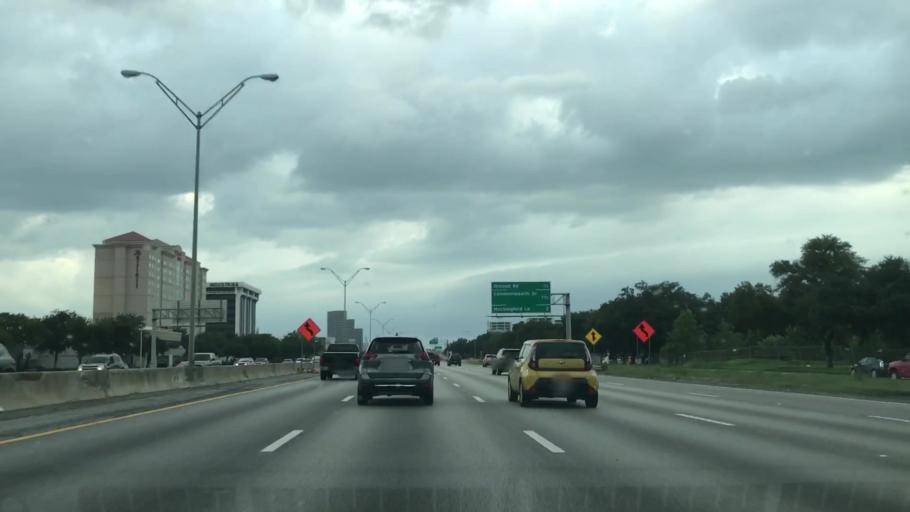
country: US
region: Texas
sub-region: Dallas County
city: Dallas
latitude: 32.8041
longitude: -96.8351
